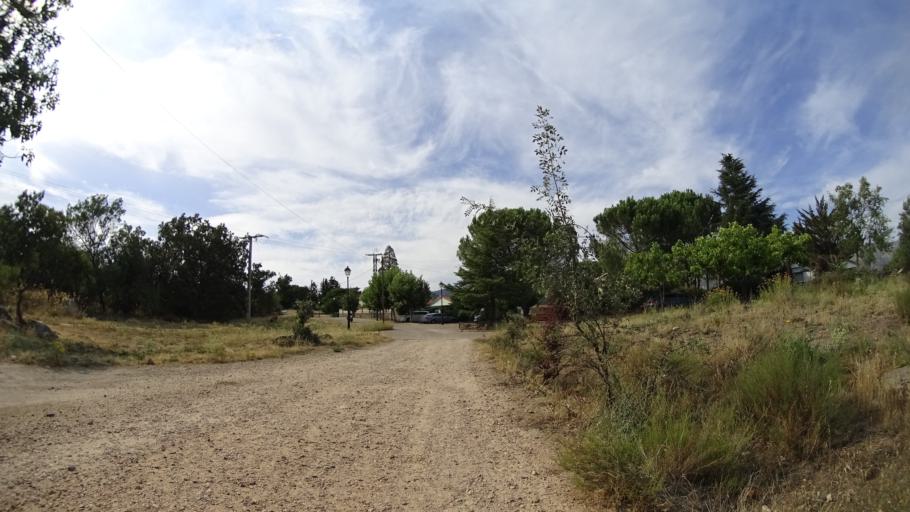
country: ES
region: Madrid
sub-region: Provincia de Madrid
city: Becerril de la Sierra
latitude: 40.7021
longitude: -3.9853
